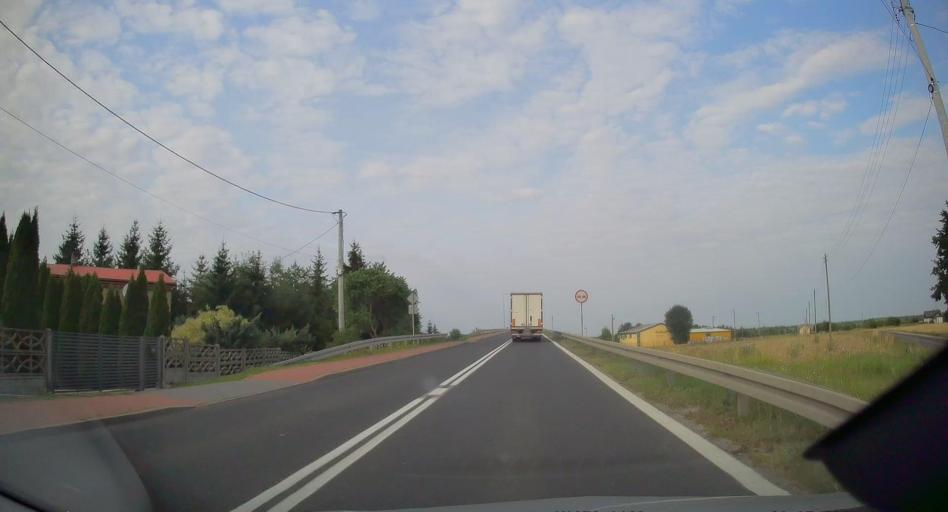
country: PL
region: Silesian Voivodeship
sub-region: Powiat czestochowski
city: Rudniki
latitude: 50.8800
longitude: 19.2490
